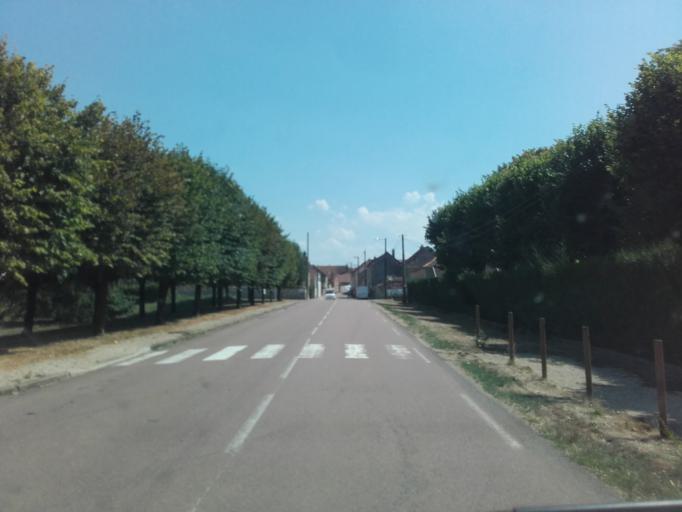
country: FR
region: Bourgogne
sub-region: Departement de l'Yonne
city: Joux-la-Ville
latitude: 47.6749
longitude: 3.8763
